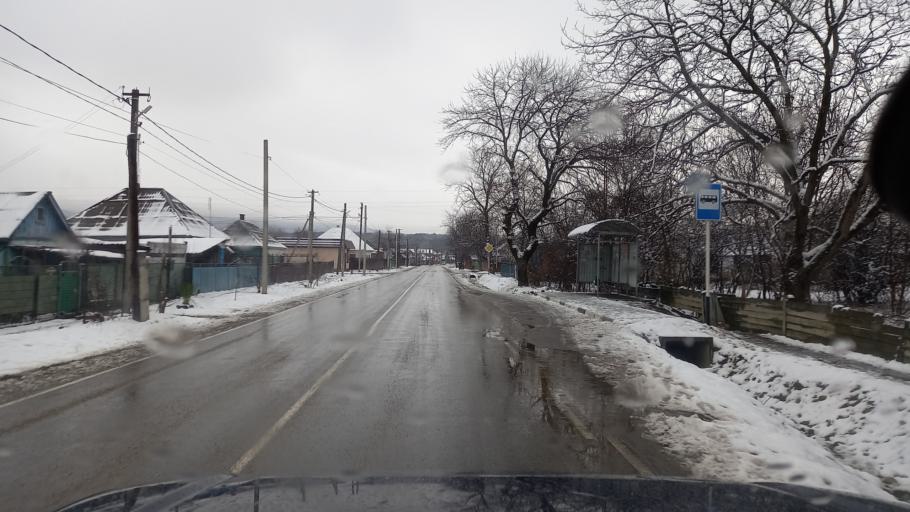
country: RU
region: Adygeya
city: Abadzekhskaya
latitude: 44.3902
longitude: 40.2214
